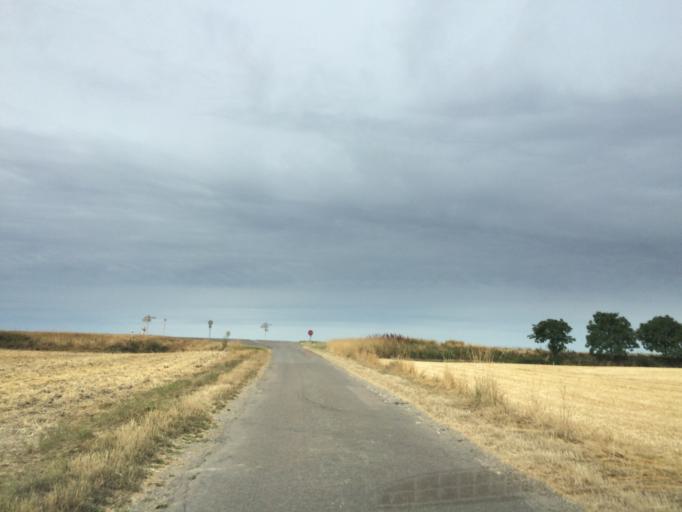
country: FR
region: Bourgogne
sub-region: Departement de l'Yonne
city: Aillant-sur-Tholon
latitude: 47.8562
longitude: 3.3739
